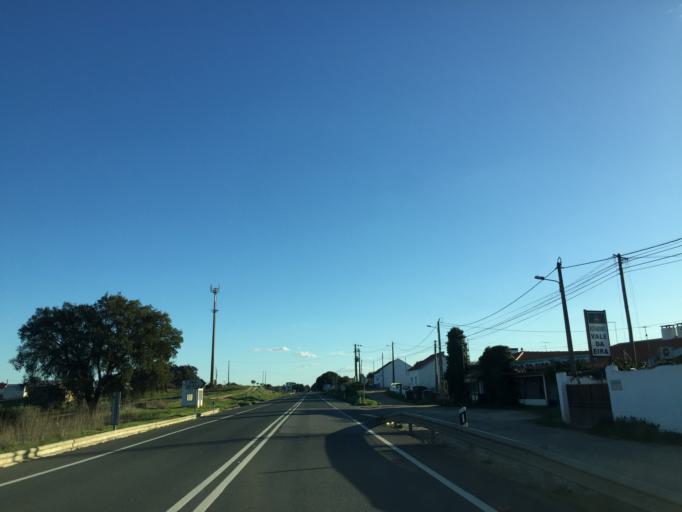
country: PT
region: Setubal
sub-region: Grandola
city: Grandola
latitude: 38.0501
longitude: -8.4023
